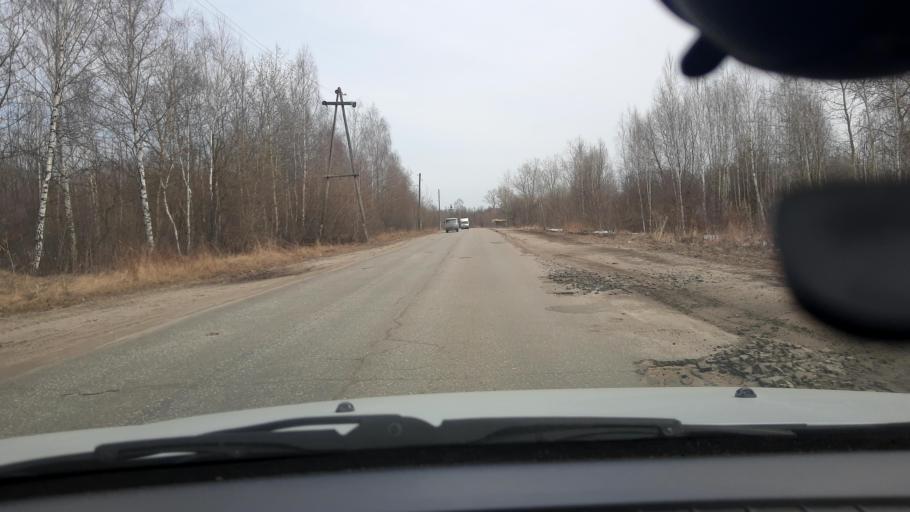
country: RU
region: Nizjnij Novgorod
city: Gidrotorf
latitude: 56.4663
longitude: 43.5512
